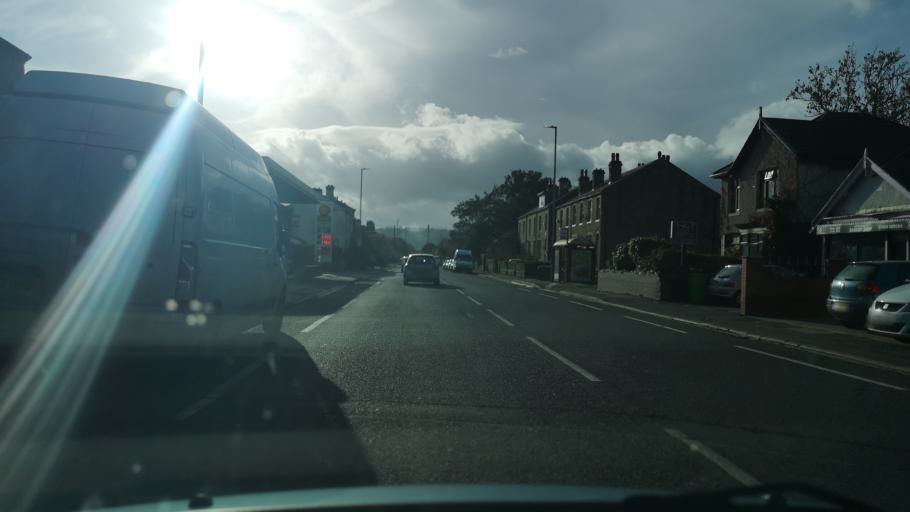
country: GB
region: England
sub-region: Kirklees
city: Mirfield
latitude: 53.6769
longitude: -1.6696
